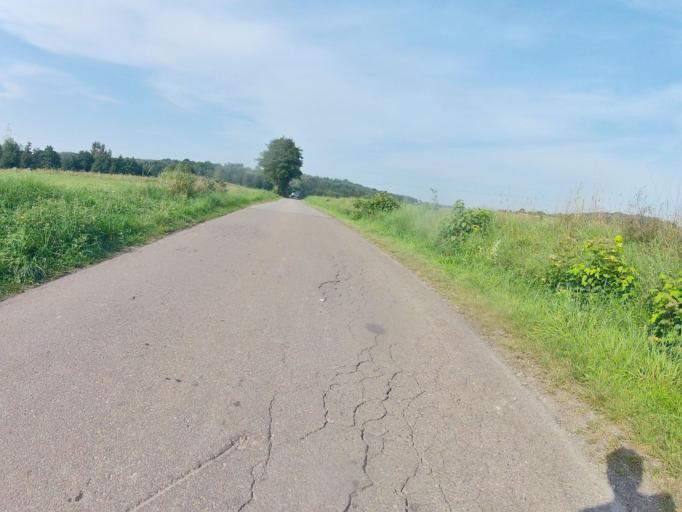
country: PL
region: Subcarpathian Voivodeship
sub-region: Powiat jasielski
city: Brzyska
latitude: 49.7927
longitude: 21.3982
